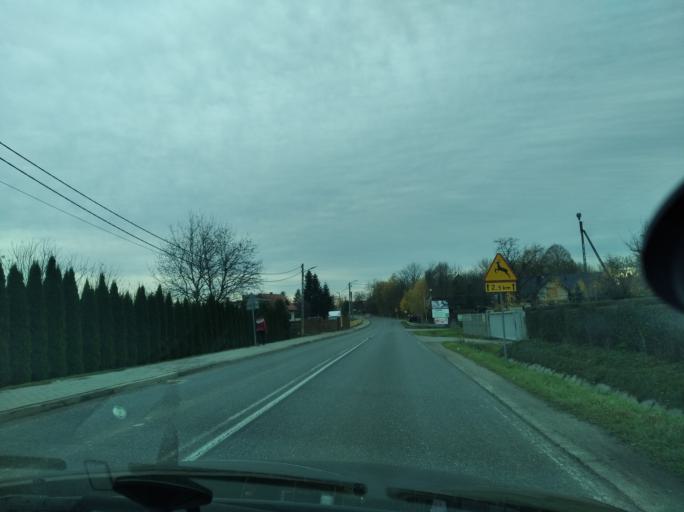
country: PL
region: Subcarpathian Voivodeship
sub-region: Powiat lancucki
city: Markowa
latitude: 50.0251
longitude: 22.3325
